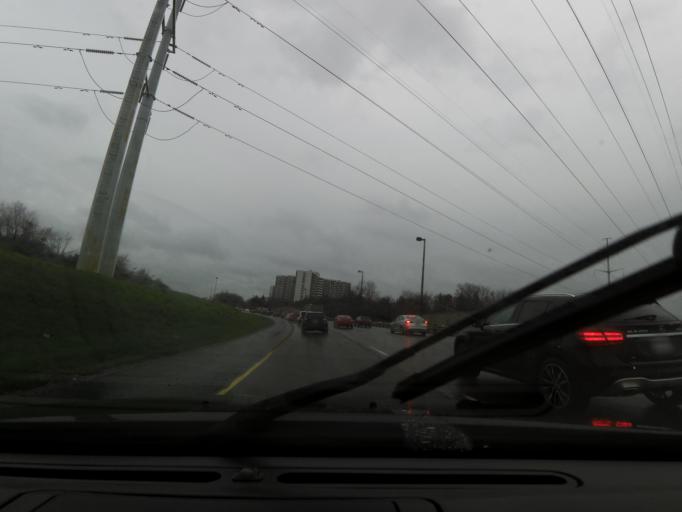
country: CA
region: Ontario
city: Scarborough
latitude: 43.7122
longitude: -79.3248
